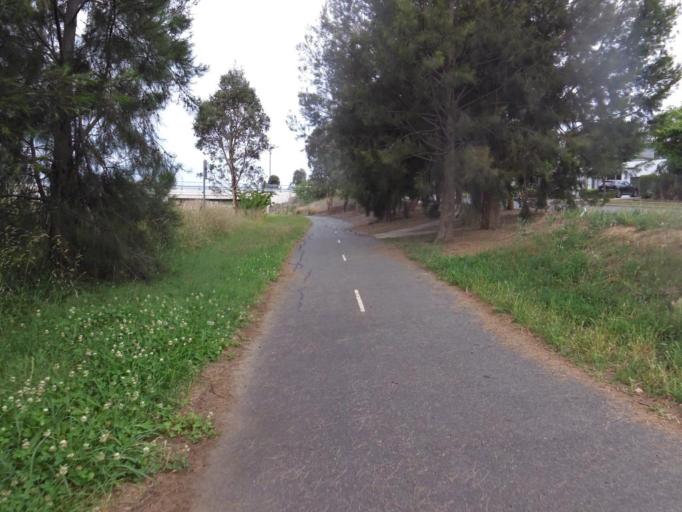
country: AU
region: Australian Capital Territory
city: Kaleen
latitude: -35.1650
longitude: 149.1428
